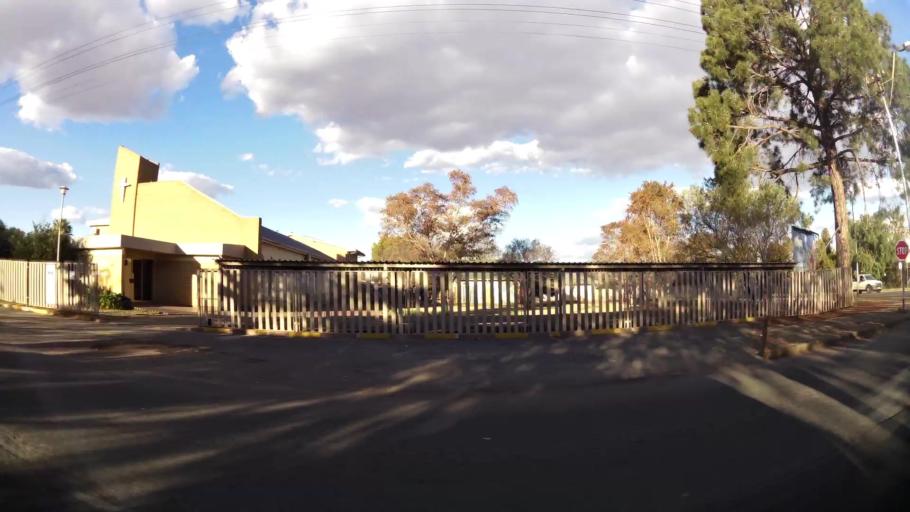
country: ZA
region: North-West
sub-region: Dr Kenneth Kaunda District Municipality
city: Potchefstroom
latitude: -26.7272
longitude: 27.0898
